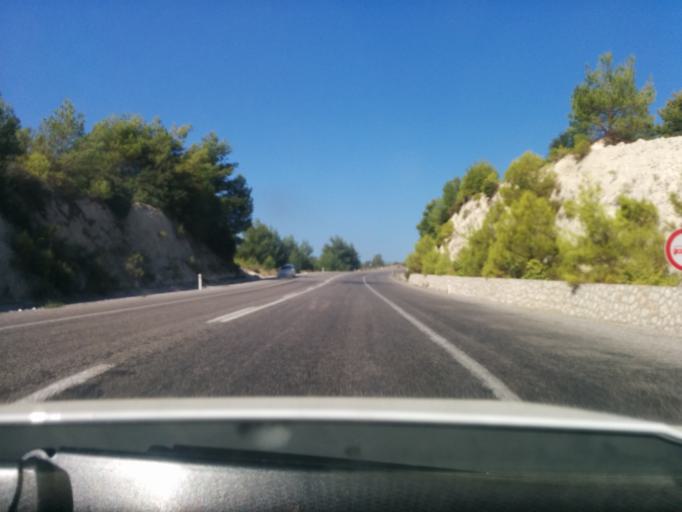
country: TR
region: Mugla
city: Esen
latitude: 36.4009
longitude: 29.3047
